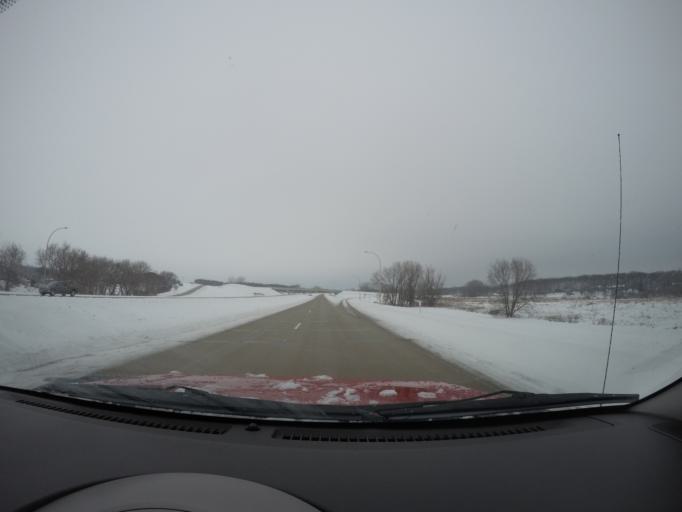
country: US
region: Minnesota
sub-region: Olmsted County
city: Rochester
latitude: 43.9571
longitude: -92.3742
